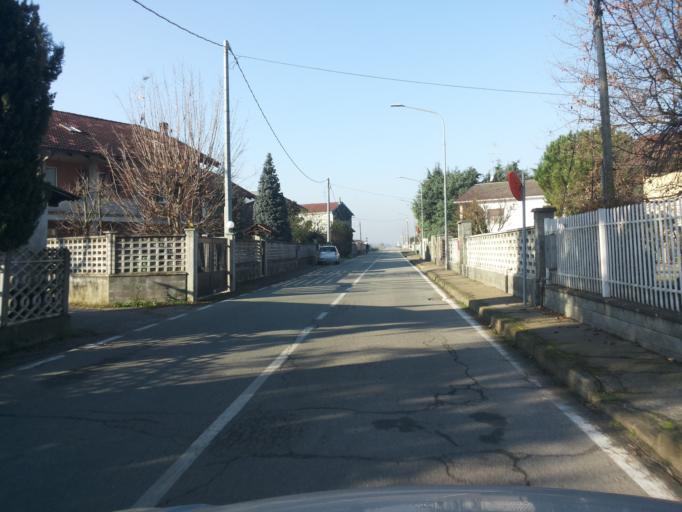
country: IT
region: Piedmont
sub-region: Provincia di Vercelli
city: Stroppiana
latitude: 45.2303
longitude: 8.4502
